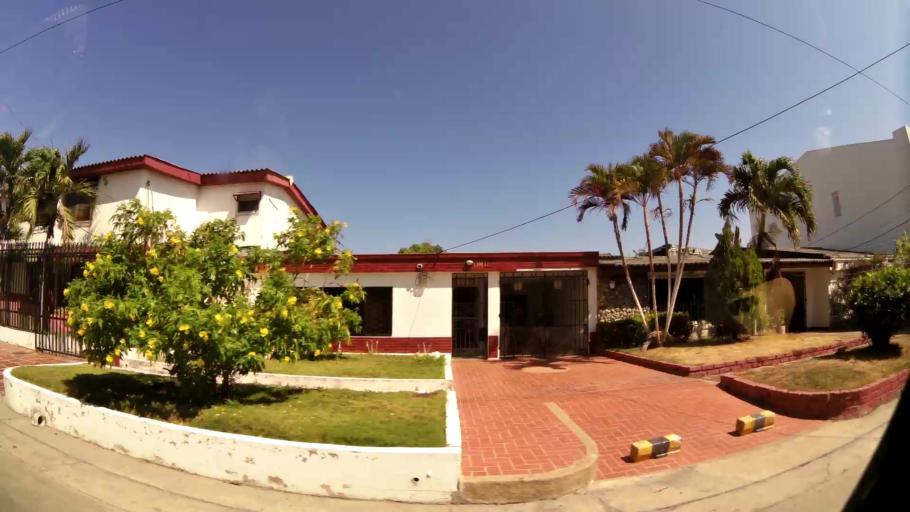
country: CO
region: Atlantico
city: Barranquilla
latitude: 11.0189
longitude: -74.8070
